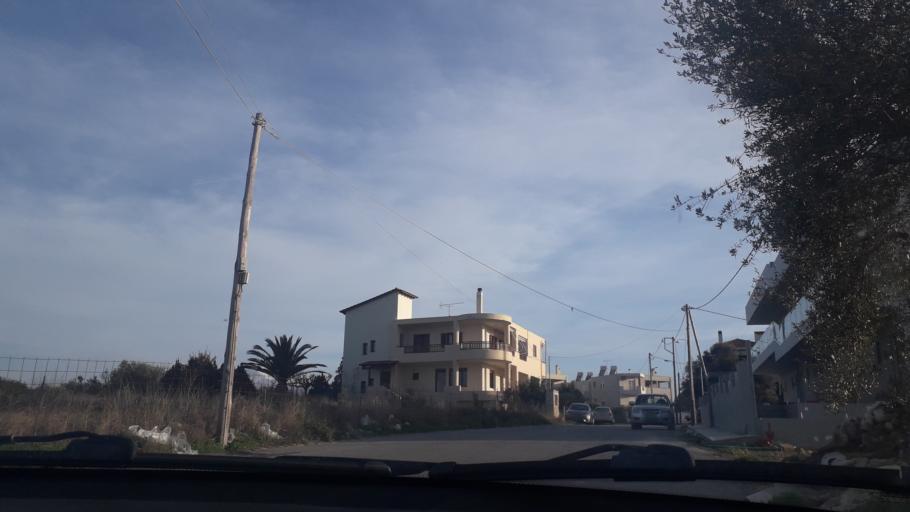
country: GR
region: Crete
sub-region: Nomos Rethymnis
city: Panormos
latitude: 35.3882
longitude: 24.6151
